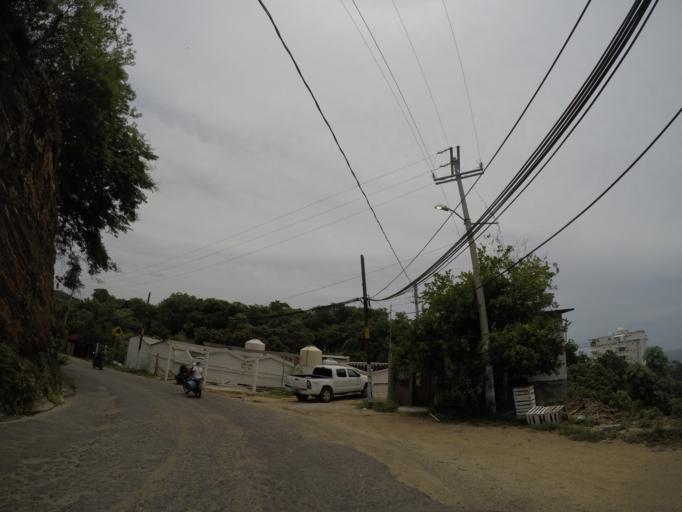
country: MX
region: Oaxaca
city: San Pedro Pochutla
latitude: 15.6669
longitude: -96.4959
